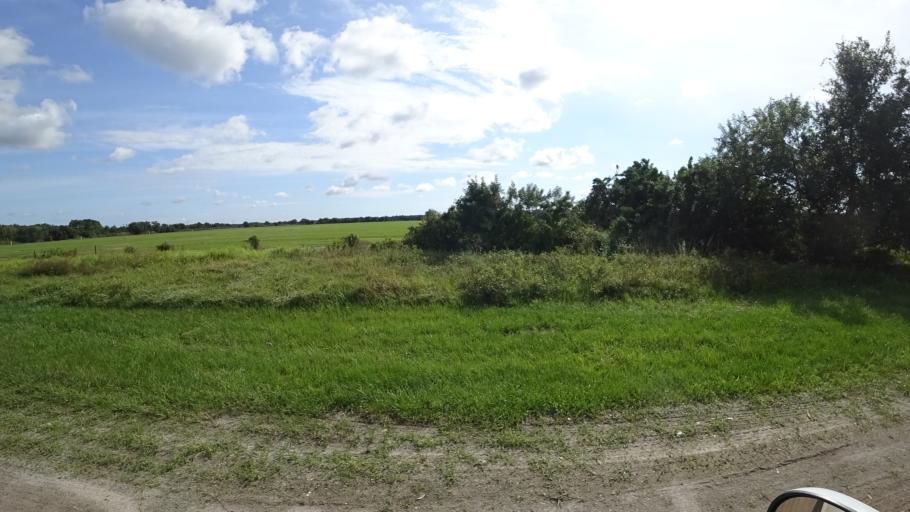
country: US
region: Florida
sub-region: Hillsborough County
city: Wimauma
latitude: 27.5957
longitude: -82.2858
